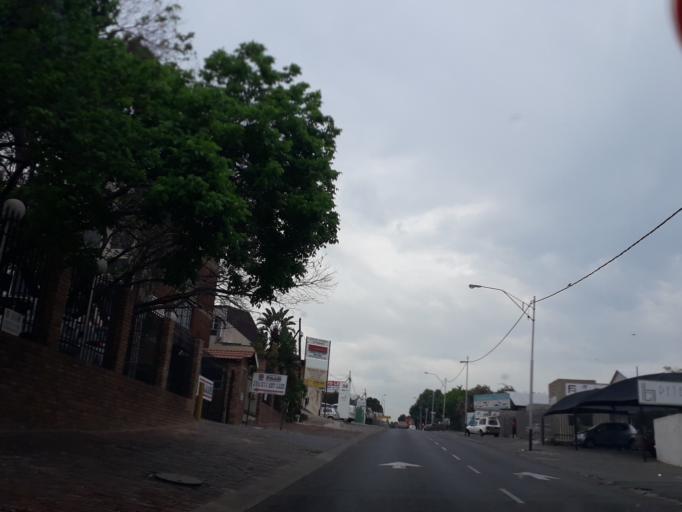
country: ZA
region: Gauteng
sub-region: City of Johannesburg Metropolitan Municipality
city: Modderfontein
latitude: -26.1076
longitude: 28.0815
